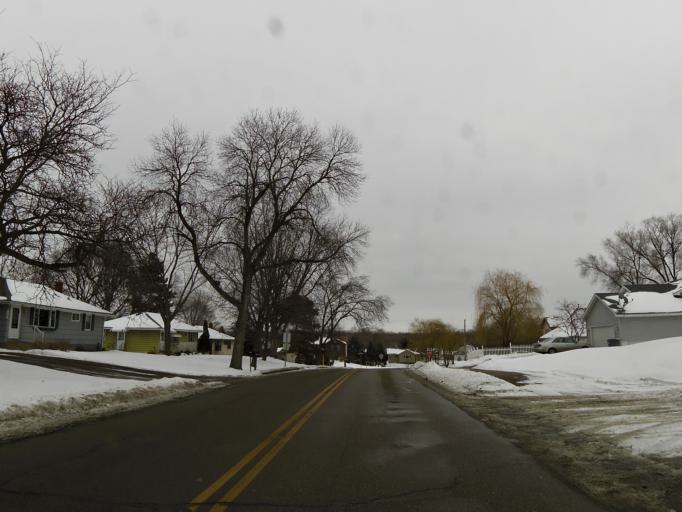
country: US
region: Minnesota
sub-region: Ramsey County
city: Little Canada
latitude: 45.0083
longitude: -93.0469
